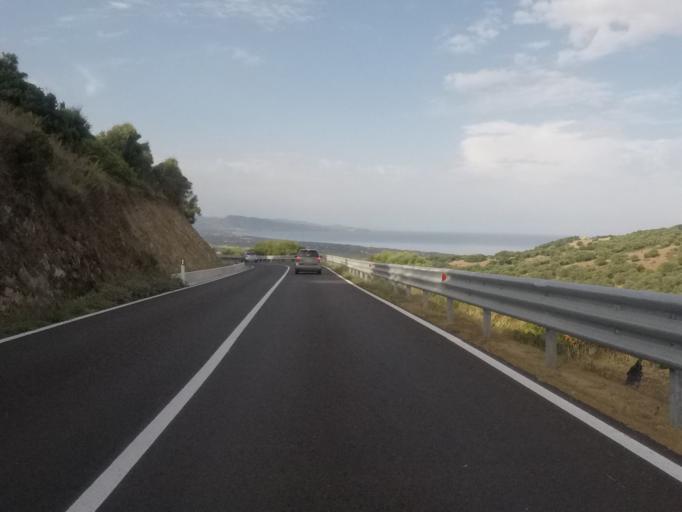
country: IT
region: Sardinia
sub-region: Provincia di Olbia-Tempio
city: Trinita d'Agultu
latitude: 40.9868
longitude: 8.8928
